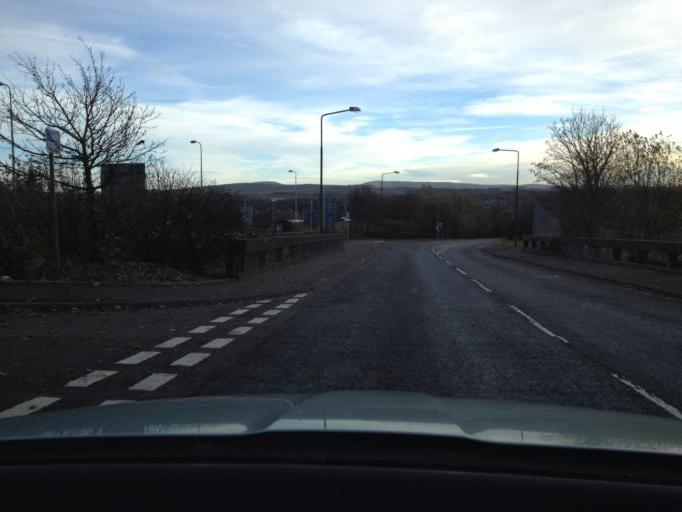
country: GB
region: Scotland
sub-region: West Lothian
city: Livingston
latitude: 55.8948
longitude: -3.5063
